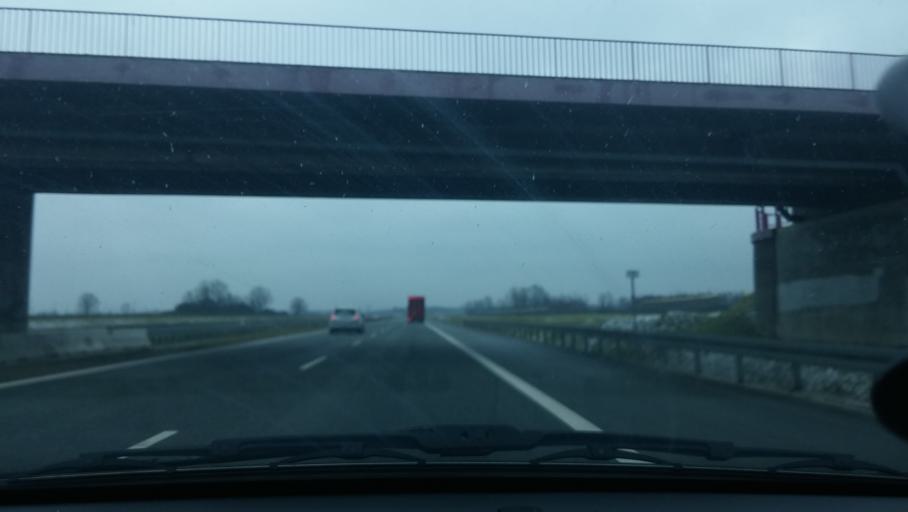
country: PL
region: Masovian Voivodeship
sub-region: Powiat minski
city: Jakubow
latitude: 52.2036
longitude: 21.7006
